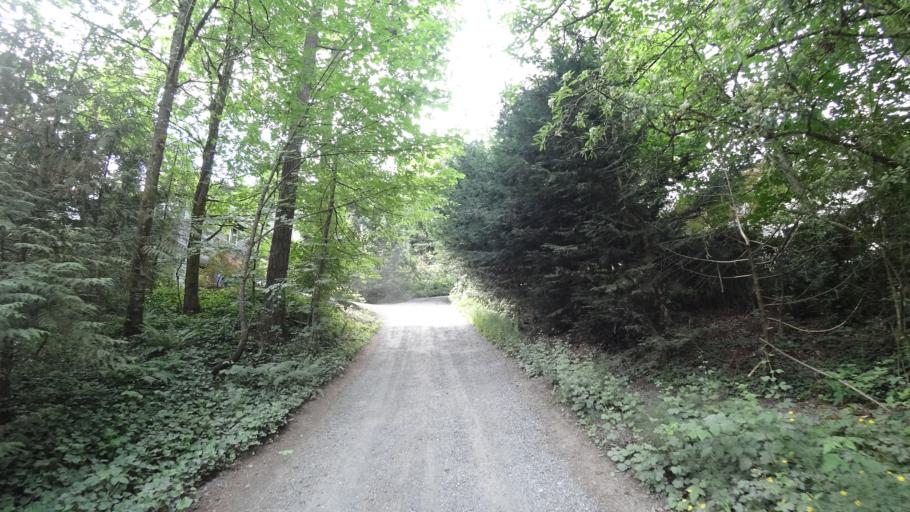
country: US
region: Oregon
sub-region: Clackamas County
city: Lake Oswego
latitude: 45.4554
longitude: -122.7024
